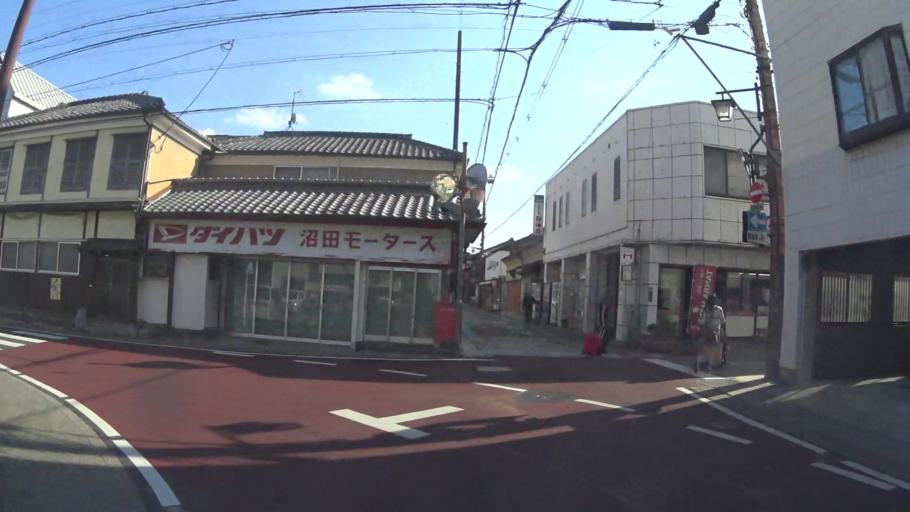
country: JP
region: Kyoto
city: Kameoka
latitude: 35.0100
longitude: 135.5806
